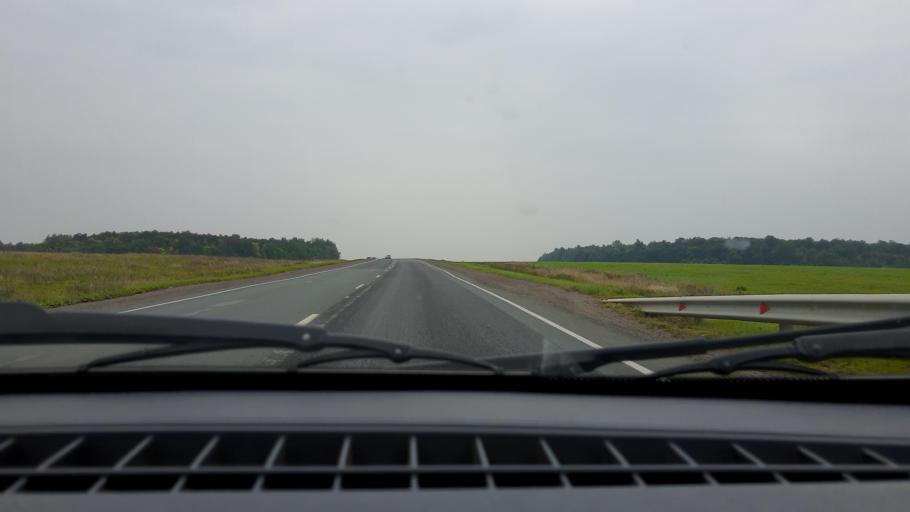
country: RU
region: Bashkortostan
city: Avdon
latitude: 54.7578
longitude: 55.7813
